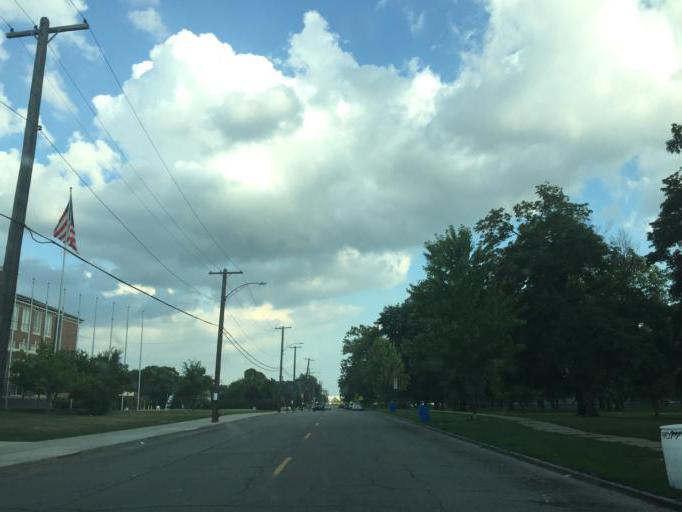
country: US
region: Michigan
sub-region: Wayne County
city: Detroit
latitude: 42.3192
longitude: -83.0927
